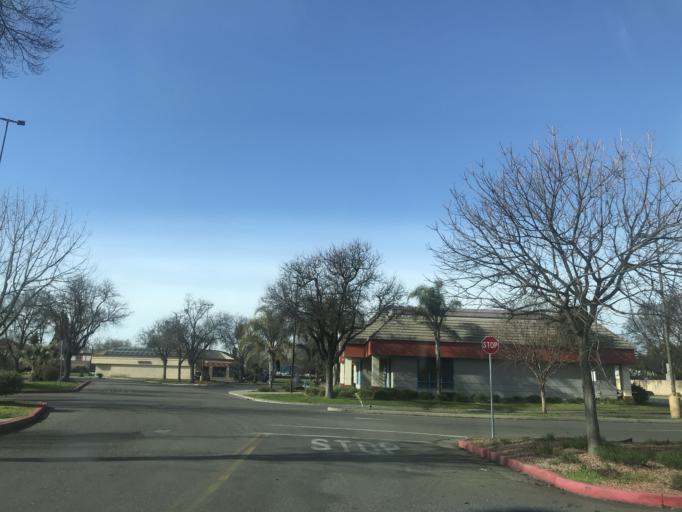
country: US
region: California
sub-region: Yolo County
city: Woodland
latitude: 38.6625
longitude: -121.7637
